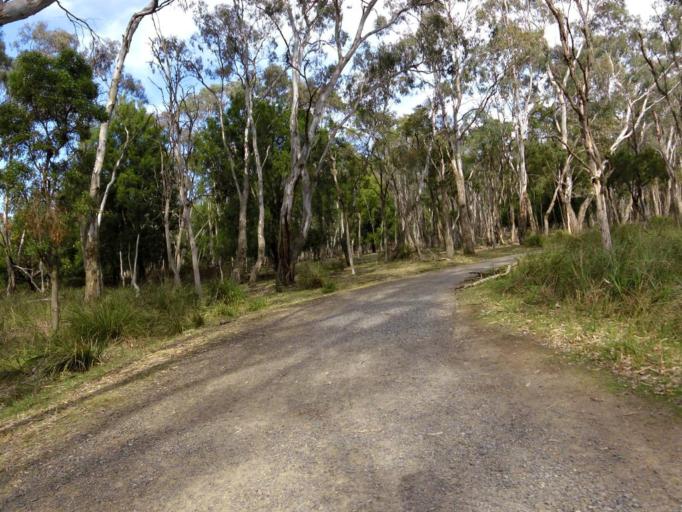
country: AU
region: Victoria
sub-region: Yarra Ranges
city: Lysterfield
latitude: -37.9562
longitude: 145.3000
